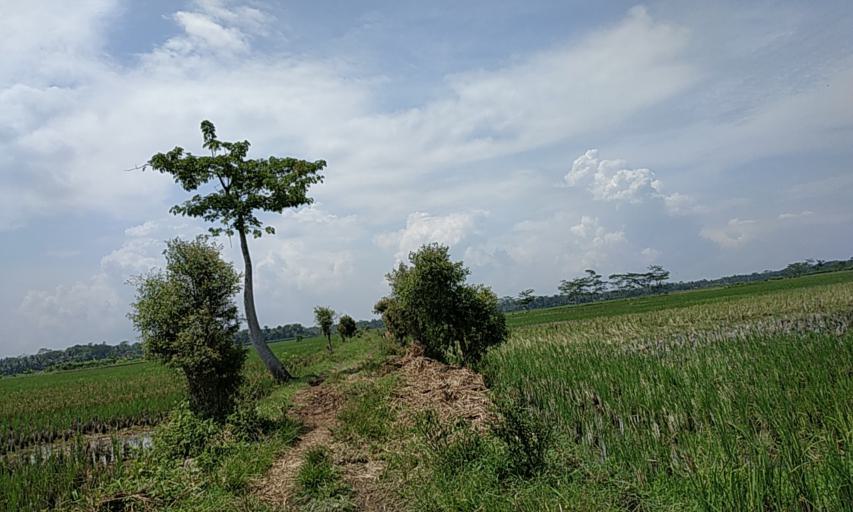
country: ID
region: Central Java
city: Kedungbulu
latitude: -7.5306
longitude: 108.7890
